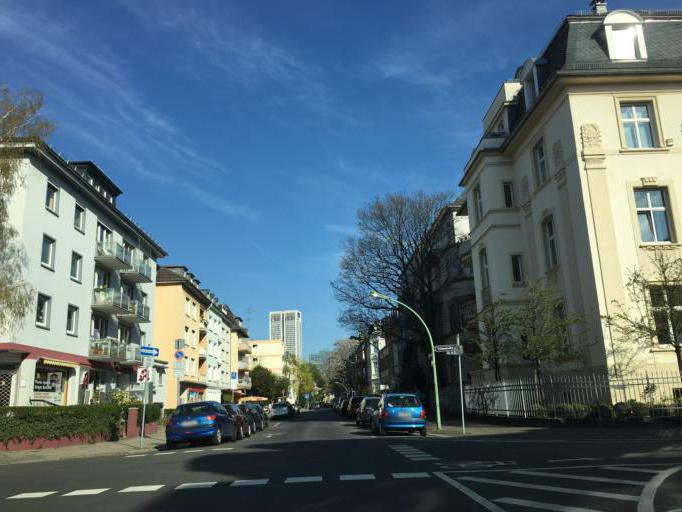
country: DE
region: Hesse
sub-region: Regierungsbezirk Darmstadt
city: Frankfurt am Main
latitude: 50.1165
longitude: 8.6546
